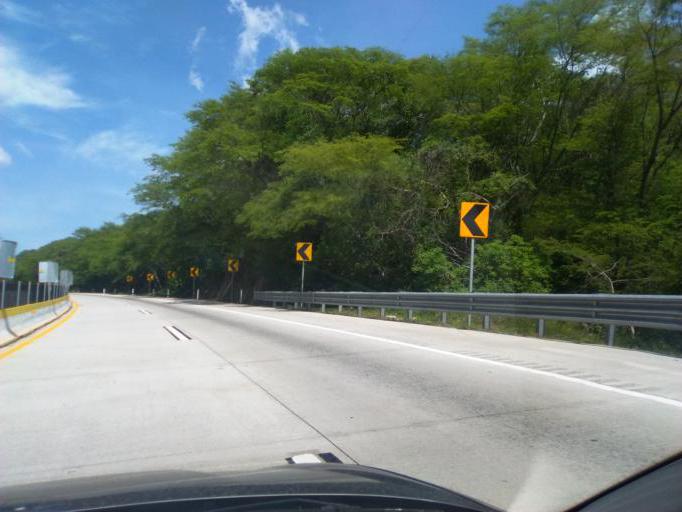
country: MX
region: Guerrero
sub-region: Acapulco de Juarez
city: Colonia Nueva Revolucion
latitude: 16.9344
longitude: -99.7822
